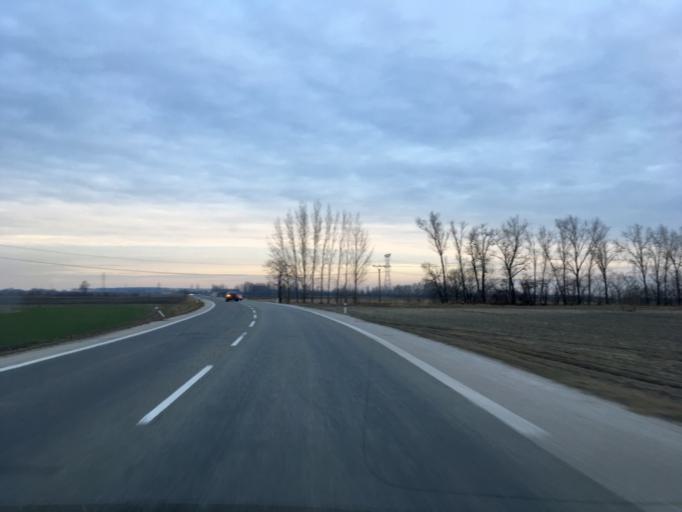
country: SK
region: Trnavsky
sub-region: Okres Dunajska Streda
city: Velky Meder
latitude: 47.8879
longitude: 17.7427
